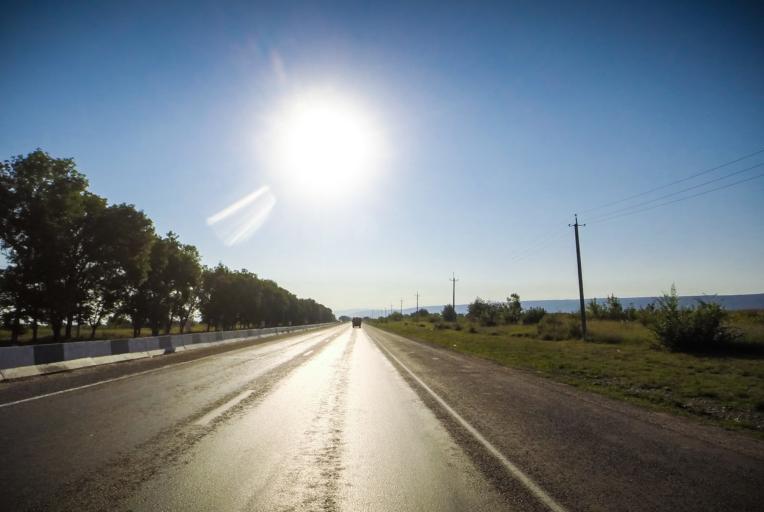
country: RU
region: Kabardino-Balkariya
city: Urukh
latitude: 43.3219
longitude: 44.0686
